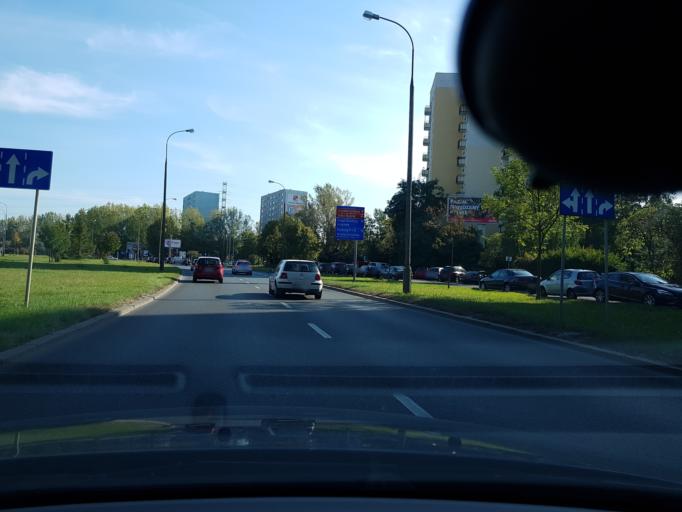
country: PL
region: Masovian Voivodeship
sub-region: Warszawa
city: Ursynow
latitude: 52.1578
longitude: 21.0424
